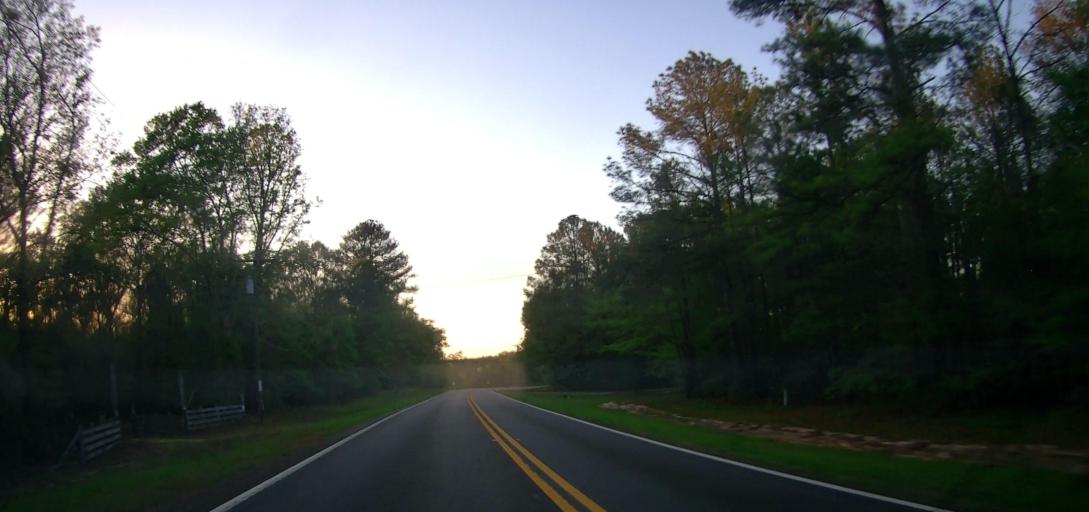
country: US
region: Georgia
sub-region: Marion County
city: Buena Vista
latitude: 32.4285
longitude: -84.5964
